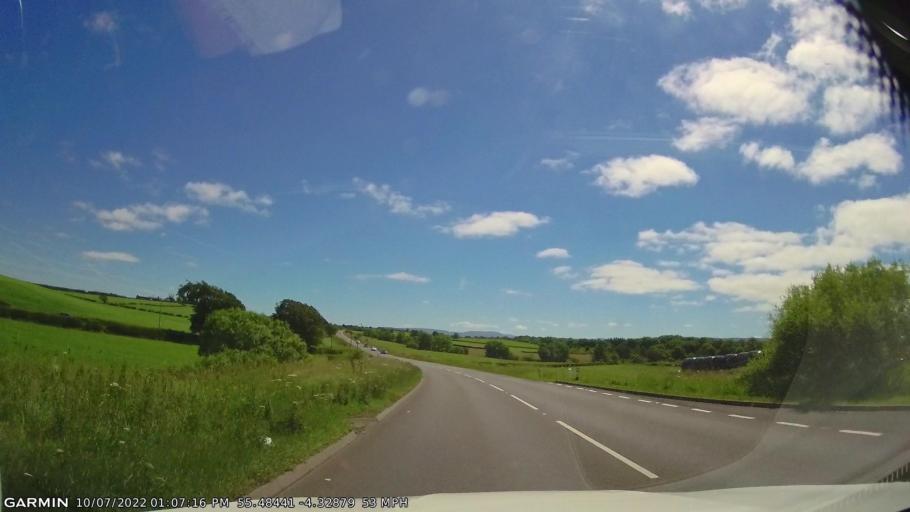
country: GB
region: Scotland
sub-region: East Ayrshire
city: Catrine
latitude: 55.4841
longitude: -4.3283
